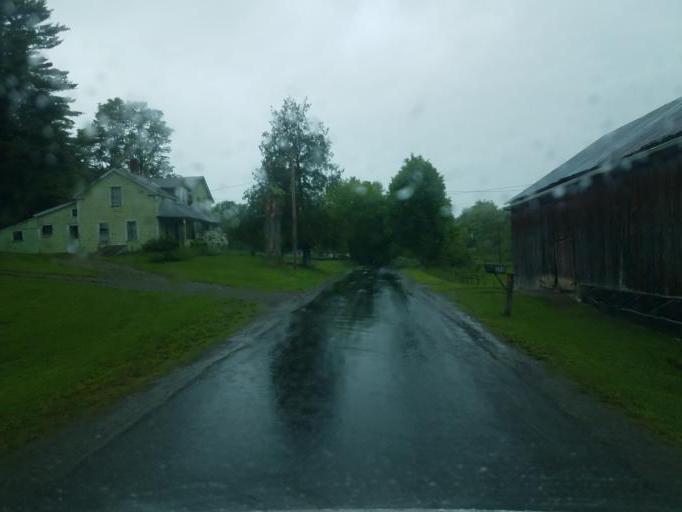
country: US
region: New York
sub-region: Herkimer County
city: Ilion
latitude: 42.9626
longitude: -75.0352
